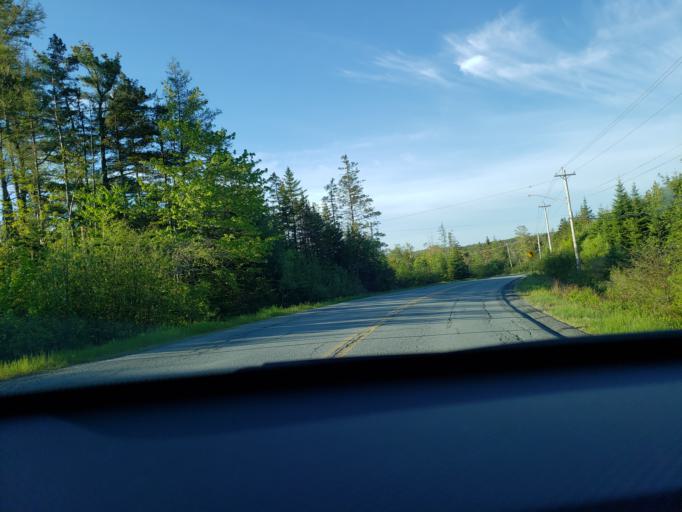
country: CA
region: Nova Scotia
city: Cole Harbour
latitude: 44.7178
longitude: -63.3971
